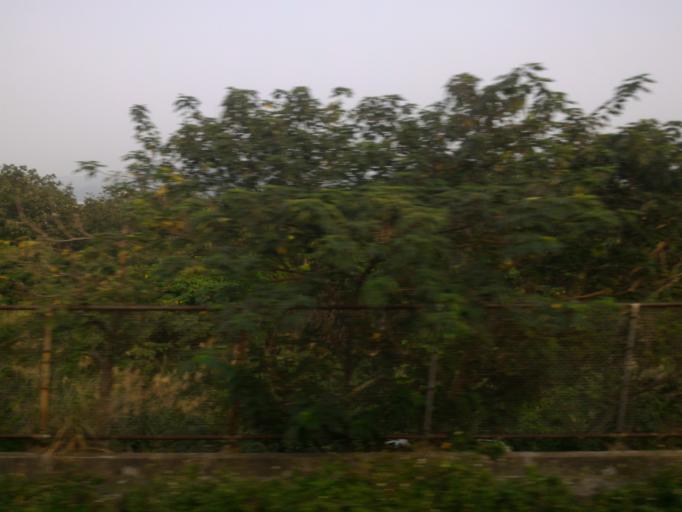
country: TW
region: Taiwan
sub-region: Taoyuan
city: Taoyuan
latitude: 24.9632
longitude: 121.3380
